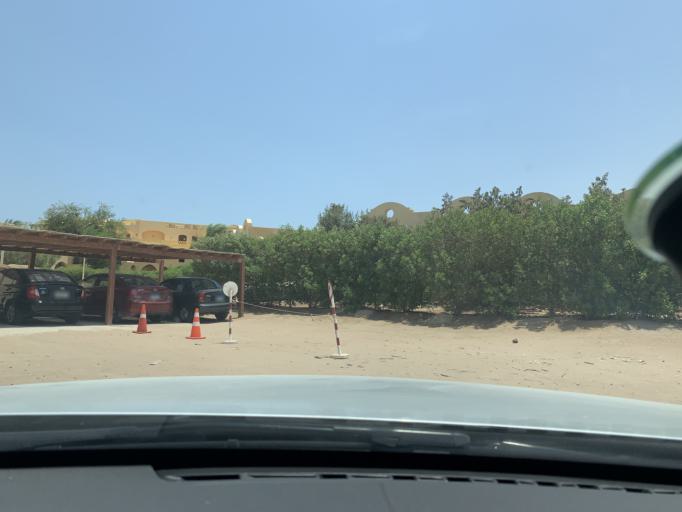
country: EG
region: Red Sea
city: El Gouna
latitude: 27.4006
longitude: 33.6722
